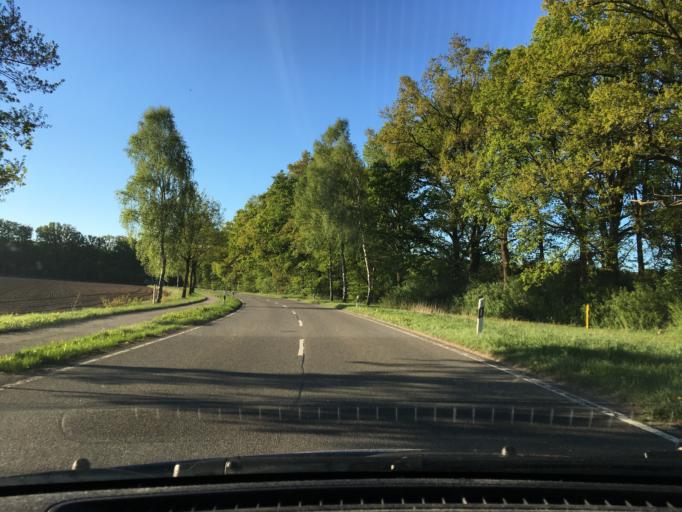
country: DE
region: Lower Saxony
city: Bispingen
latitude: 53.0306
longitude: 10.0000
